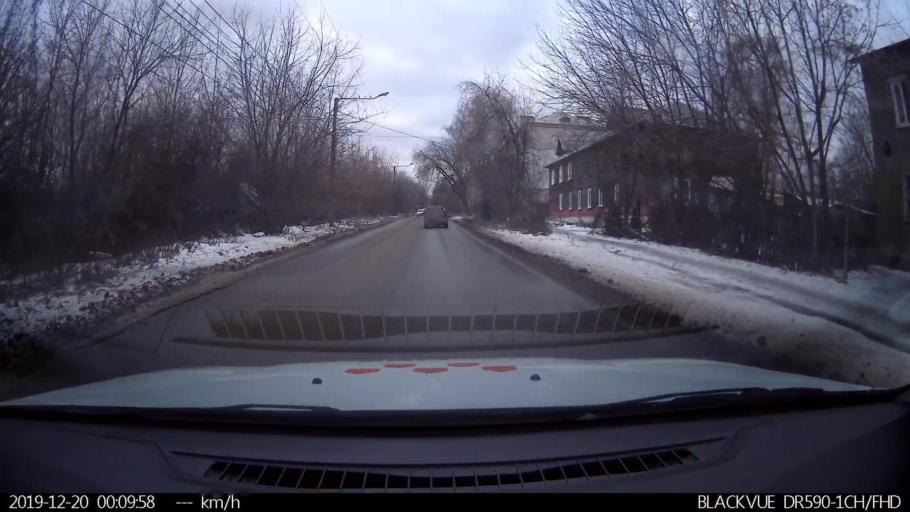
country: RU
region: Jaroslavl
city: Yaroslavl
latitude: 57.6511
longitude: 39.7495
